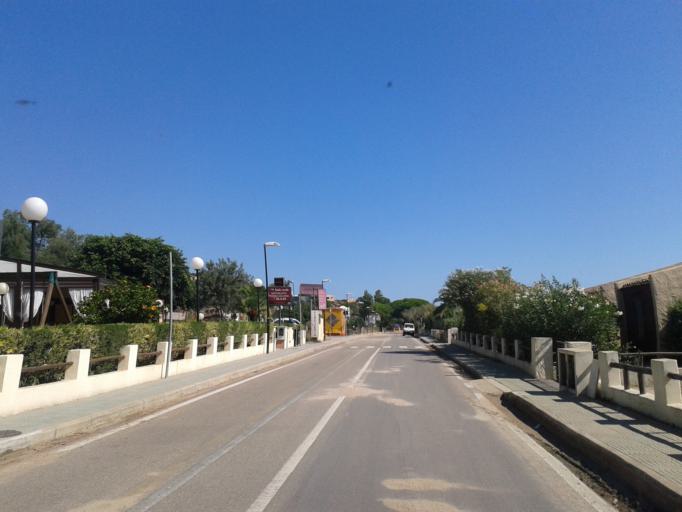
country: IT
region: Sardinia
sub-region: Provincia di Cagliari
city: Olia Speciosa
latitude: 39.2496
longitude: 9.5714
